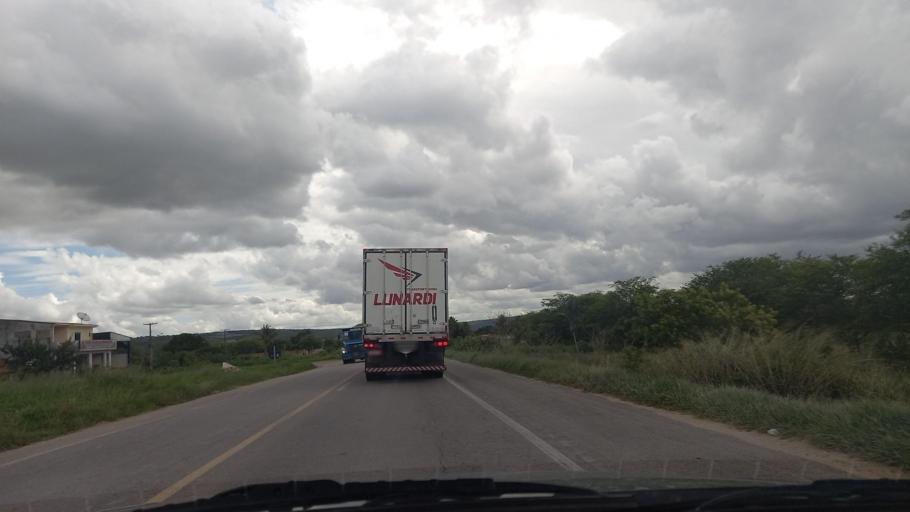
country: BR
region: Pernambuco
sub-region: Lajedo
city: Lajedo
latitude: -8.6617
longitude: -36.3439
